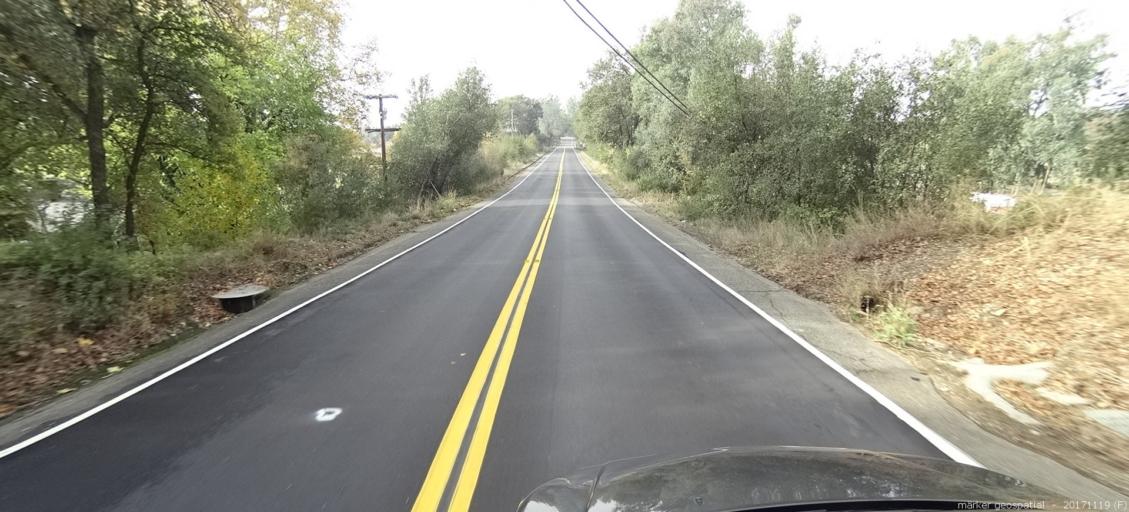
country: US
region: California
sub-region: Shasta County
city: Anderson
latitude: 40.4984
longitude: -122.3130
